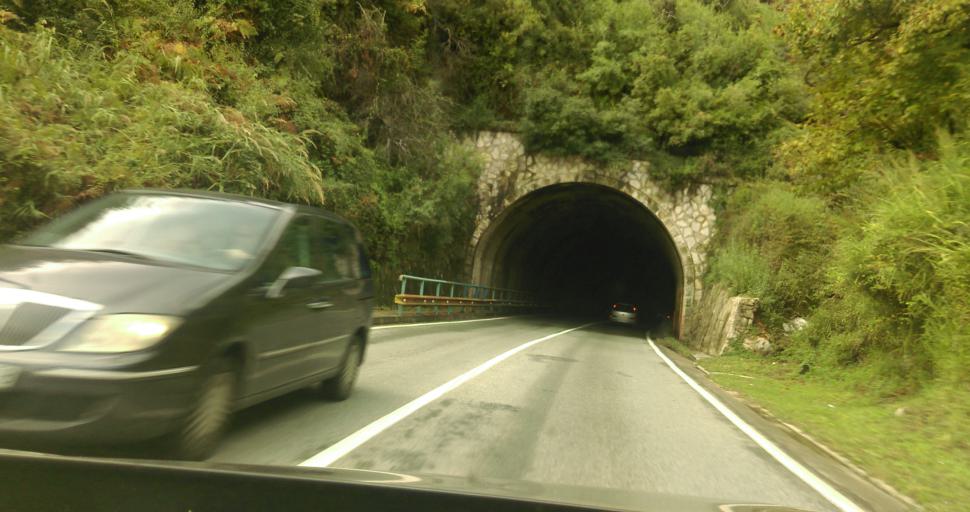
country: ME
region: Budva
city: Budva
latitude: 42.2780
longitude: 18.8255
